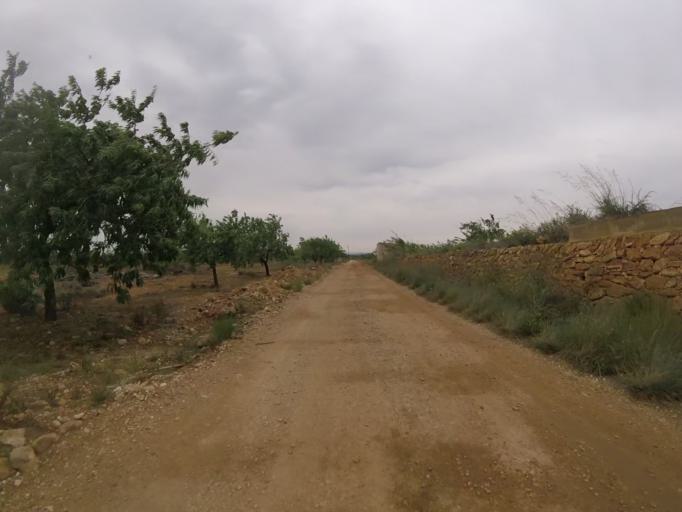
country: ES
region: Valencia
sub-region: Provincia de Castello
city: Alcoceber
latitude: 40.2658
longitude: 0.2563
